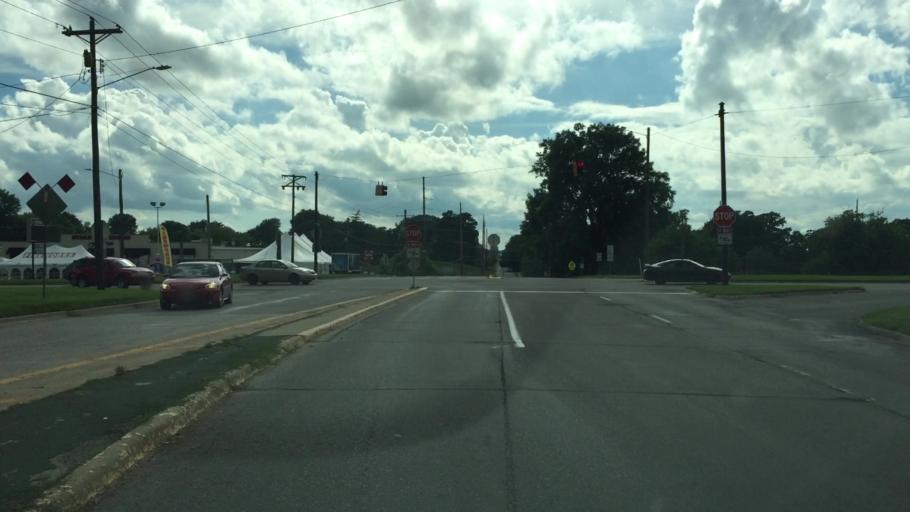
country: US
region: Iowa
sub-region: Jasper County
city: Newton
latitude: 41.6991
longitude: -93.0750
